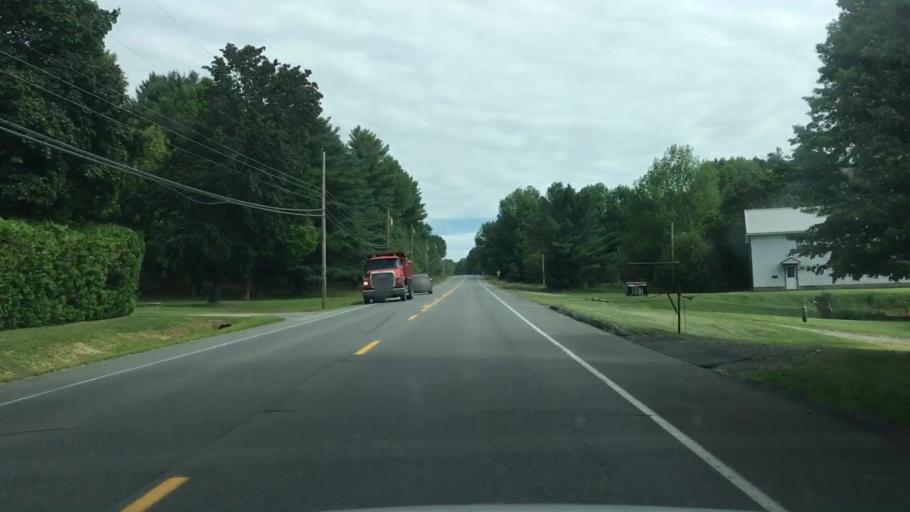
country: US
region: Maine
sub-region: Piscataquis County
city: Dover-Foxcroft
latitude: 45.2086
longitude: -69.1775
